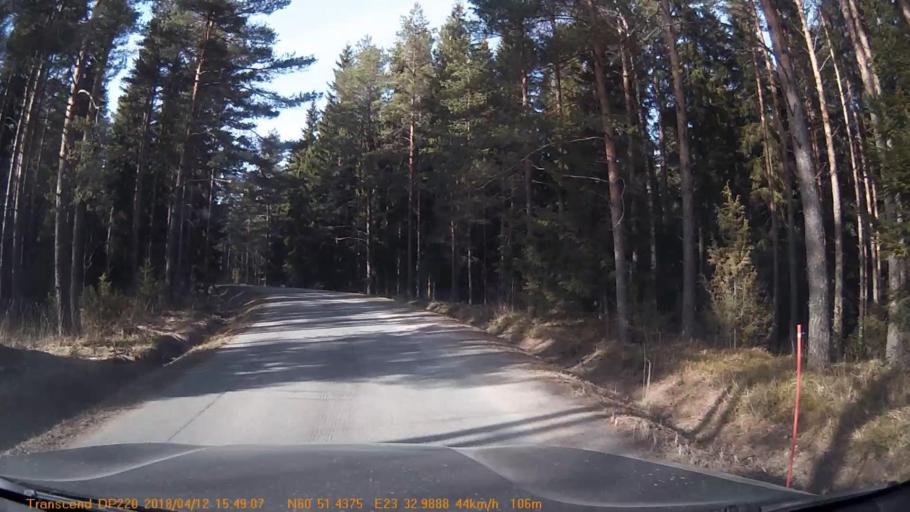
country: FI
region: Haeme
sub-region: Forssa
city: Forssa
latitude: 60.8574
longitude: 23.5498
